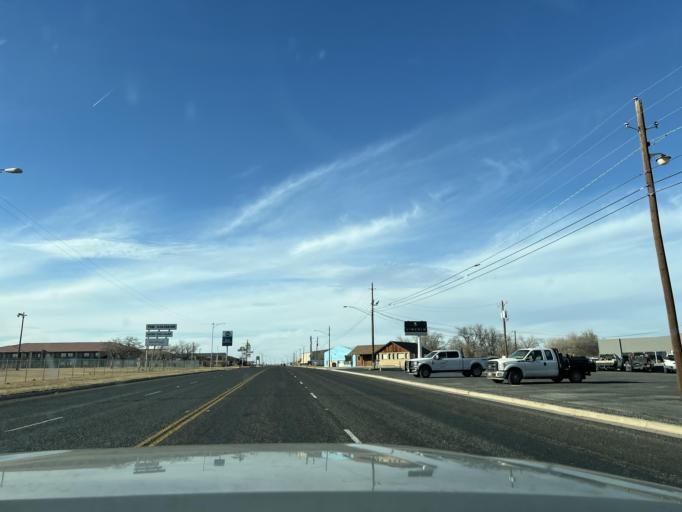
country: US
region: Texas
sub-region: Scurry County
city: Snyder
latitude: 32.7070
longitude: -100.8859
